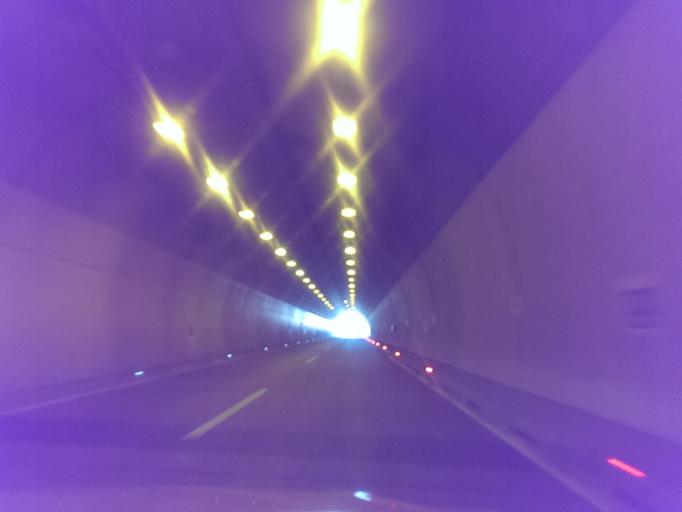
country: AT
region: Upper Austria
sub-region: Politischer Bezirk Kirchdorf an der Krems
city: Rossleithen
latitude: 47.7660
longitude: 14.1926
